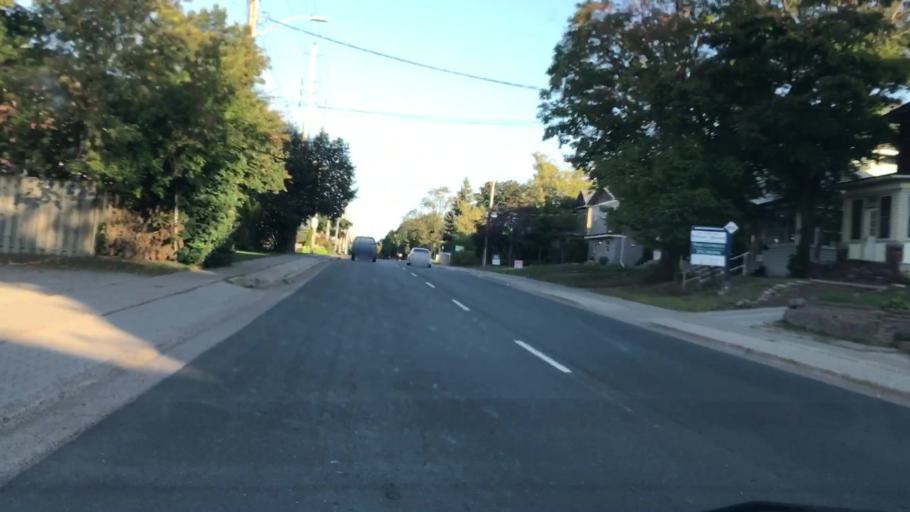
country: CA
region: Ontario
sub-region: Algoma
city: Sault Ste. Marie
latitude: 46.5103
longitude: -84.3264
